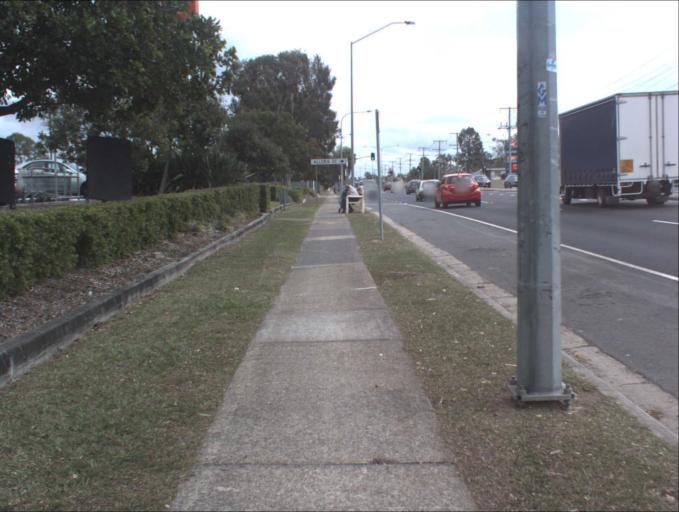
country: AU
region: Queensland
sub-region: Logan
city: Waterford West
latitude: -27.6921
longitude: 153.1356
